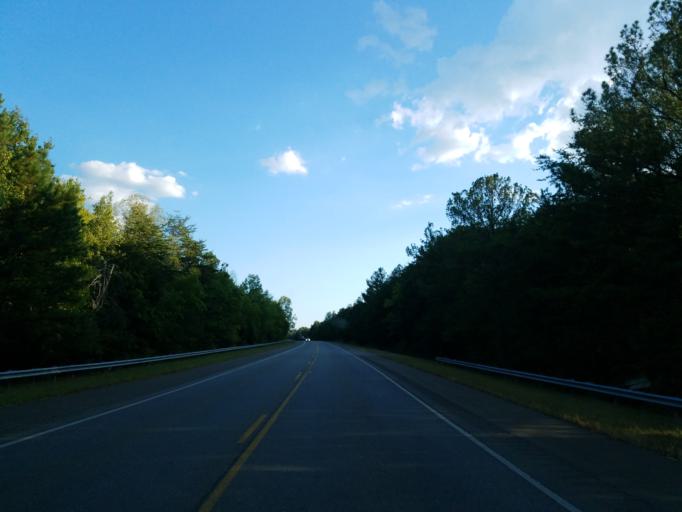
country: US
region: Georgia
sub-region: Murray County
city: Chatsworth
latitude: 34.6145
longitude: -84.7138
